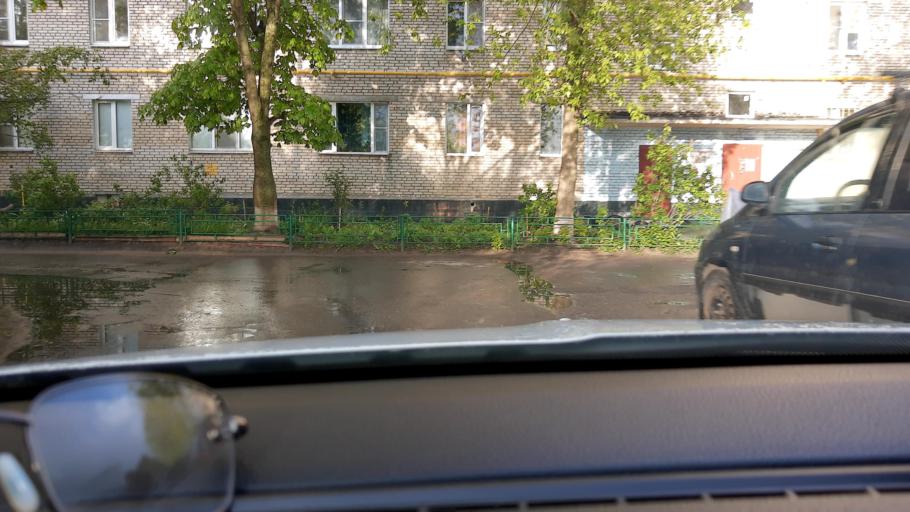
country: RU
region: Moskovskaya
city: Nakhabino
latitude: 55.8376
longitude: 37.1788
